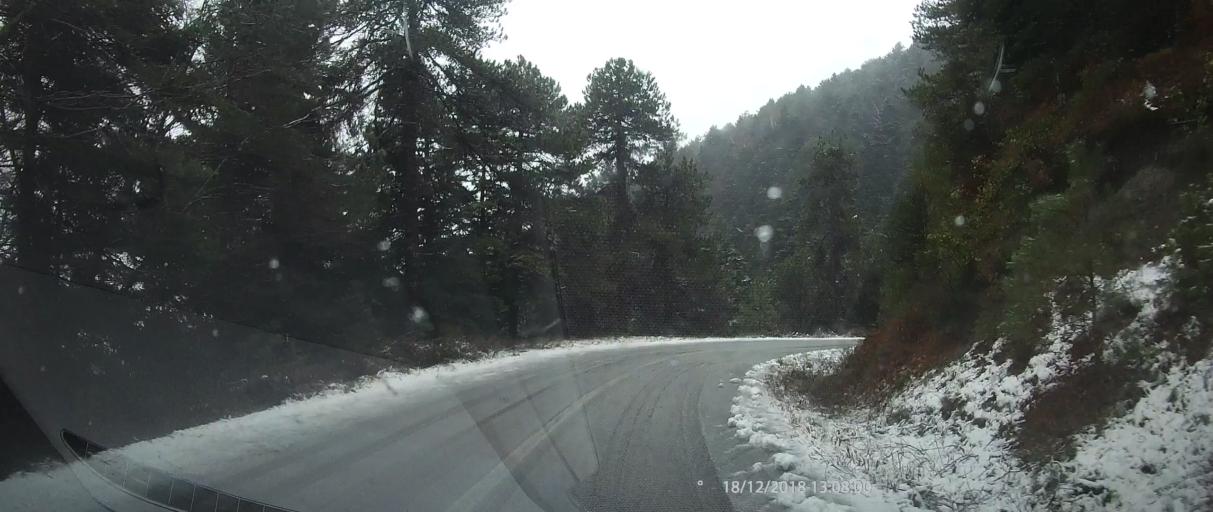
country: GR
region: Central Macedonia
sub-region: Nomos Pierias
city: Litochoro
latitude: 40.1068
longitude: 22.4754
